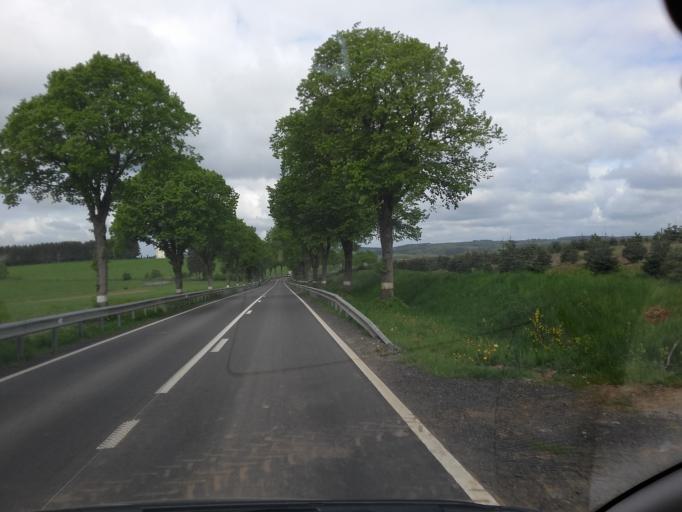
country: BE
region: Wallonia
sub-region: Province du Luxembourg
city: Neufchateau
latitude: 49.8439
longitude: 5.3909
